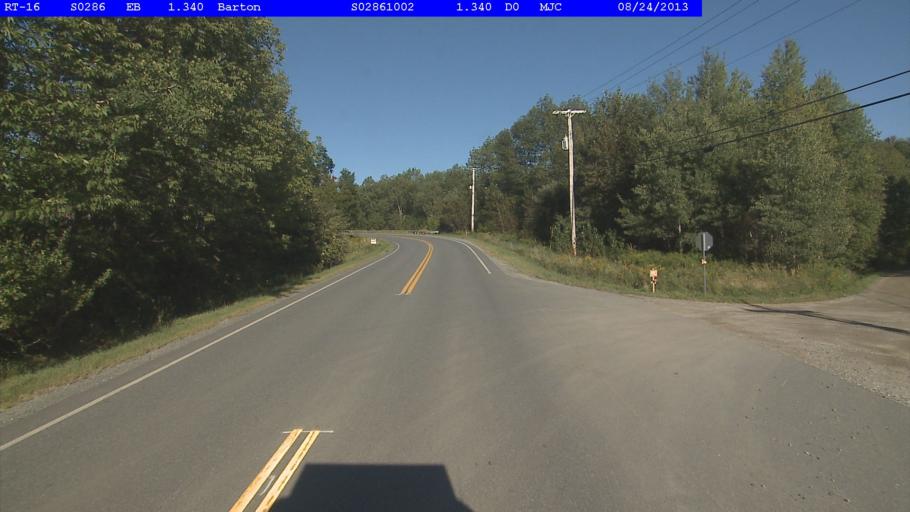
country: US
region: Vermont
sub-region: Orleans County
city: Newport
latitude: 44.7566
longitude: -72.1544
